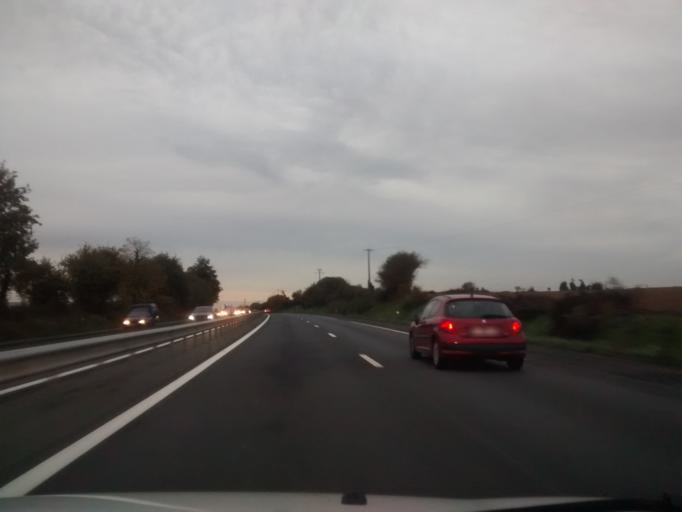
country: FR
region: Brittany
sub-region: Departement des Cotes-d'Armor
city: Broons
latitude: 48.3097
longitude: -2.2384
